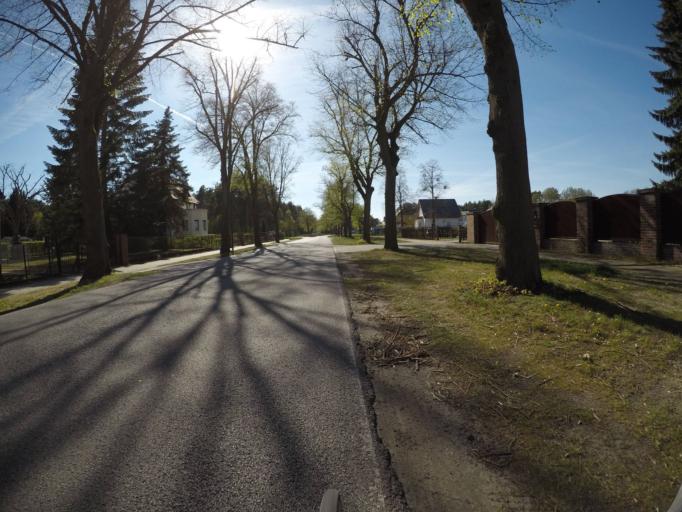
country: DE
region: Brandenburg
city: Rehfelde
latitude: 52.4566
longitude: 13.9045
